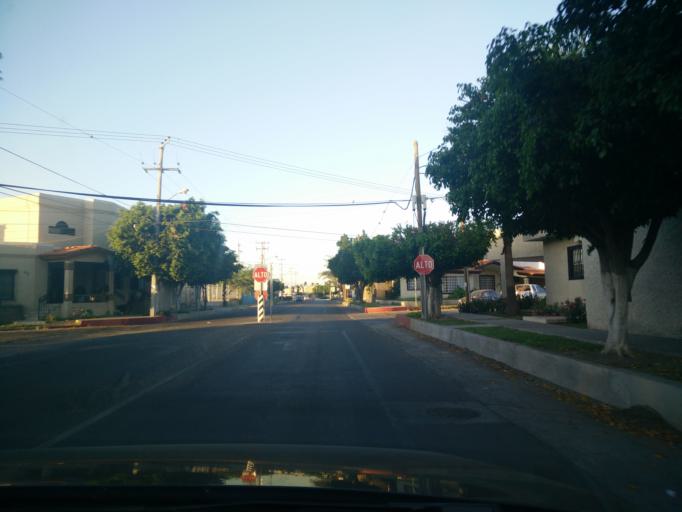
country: MX
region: Sonora
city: Hermosillo
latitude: 29.0811
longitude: -110.9845
